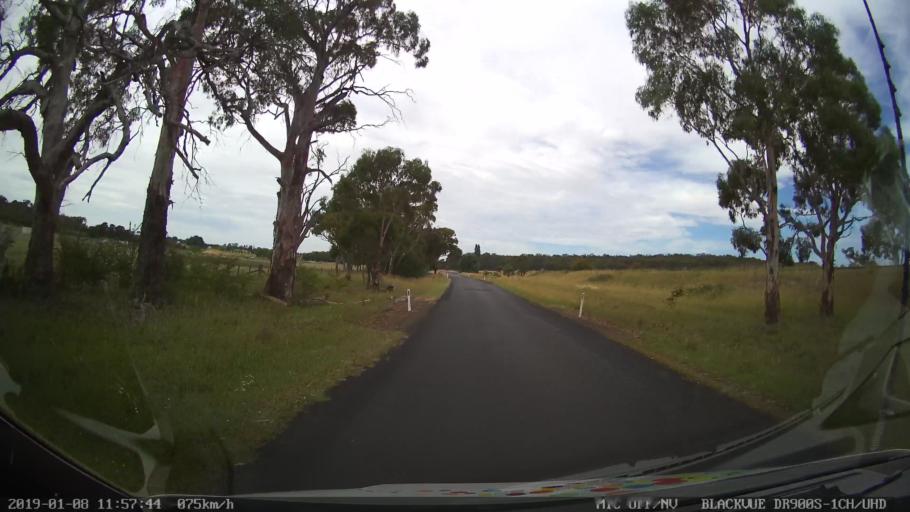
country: AU
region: New South Wales
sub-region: Armidale Dumaresq
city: Armidale
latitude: -30.4526
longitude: 151.5690
